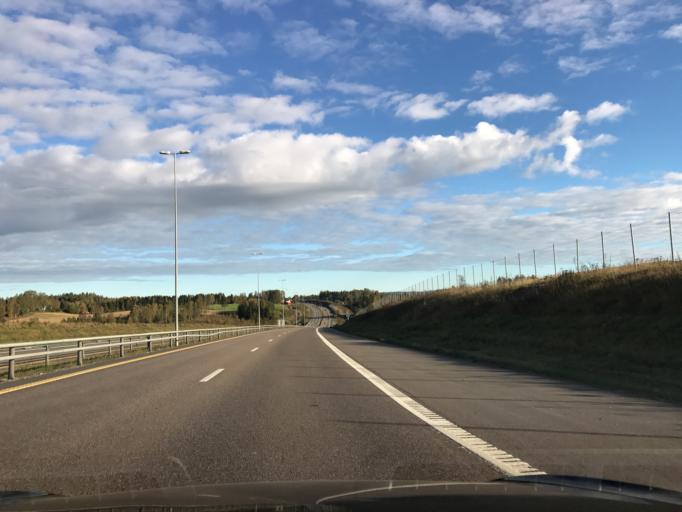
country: NO
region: Akershus
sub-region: Eidsvoll
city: Raholt
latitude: 60.2350
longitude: 11.1747
